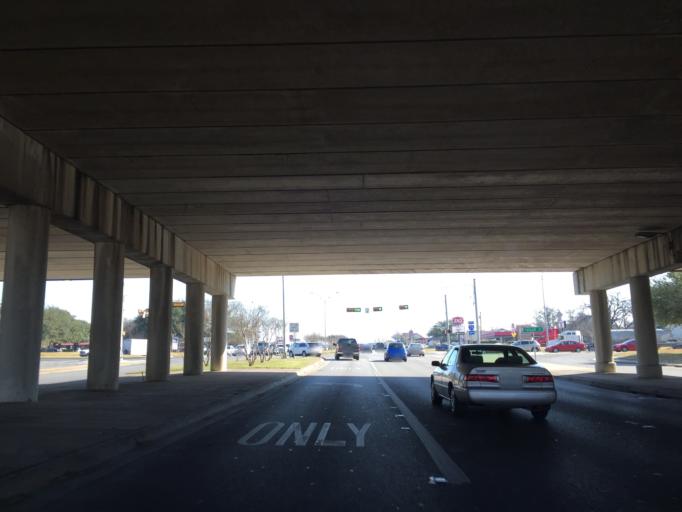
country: US
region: Texas
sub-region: Williamson County
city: Round Rock
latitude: 30.5171
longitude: -97.6881
